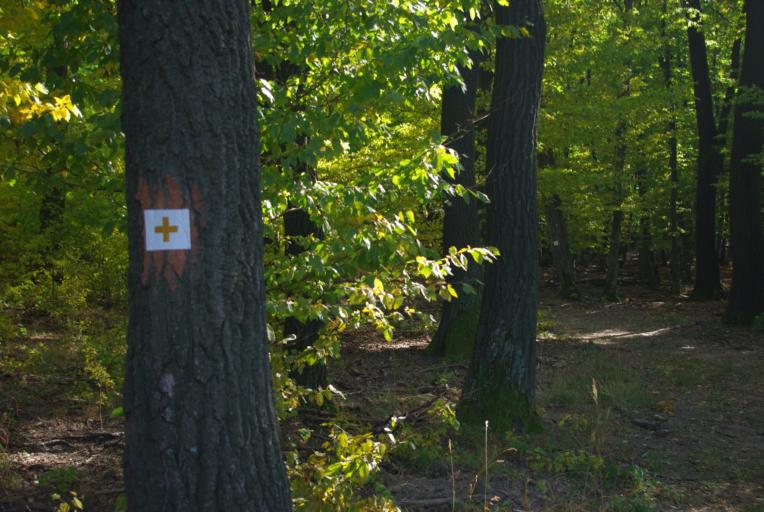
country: HU
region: Pest
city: Budakeszi
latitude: 47.5431
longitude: 18.8935
